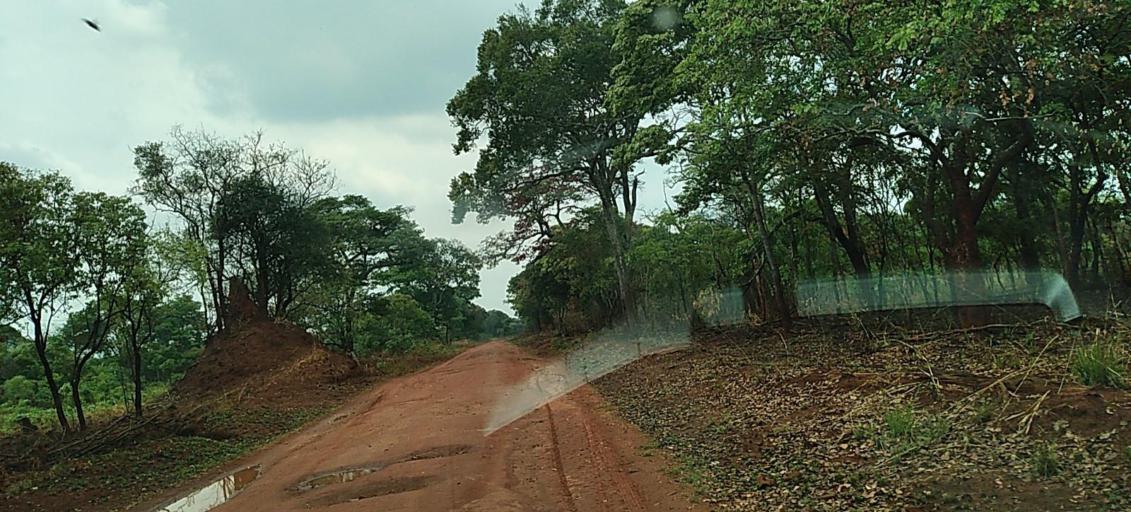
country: ZM
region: North-Western
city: Mwinilunga
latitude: -11.5481
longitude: 24.7759
